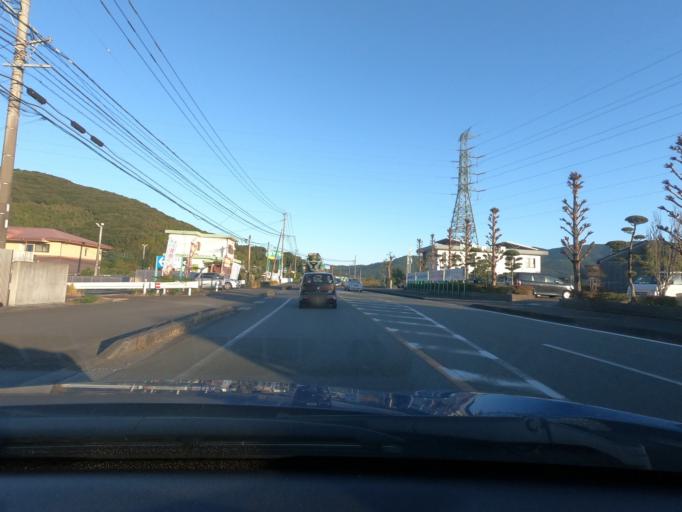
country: JP
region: Kagoshima
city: Satsumasendai
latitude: 31.8078
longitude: 130.3385
